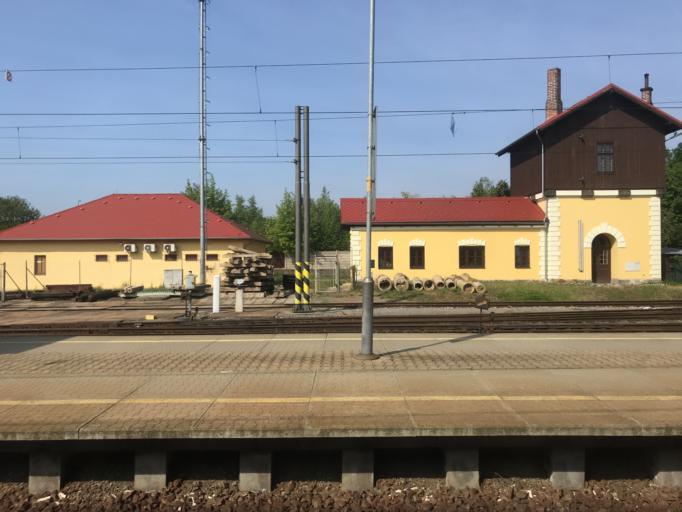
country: CZ
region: Central Bohemia
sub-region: Okres Benesov
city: Benesov
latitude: 49.7798
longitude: 14.6826
